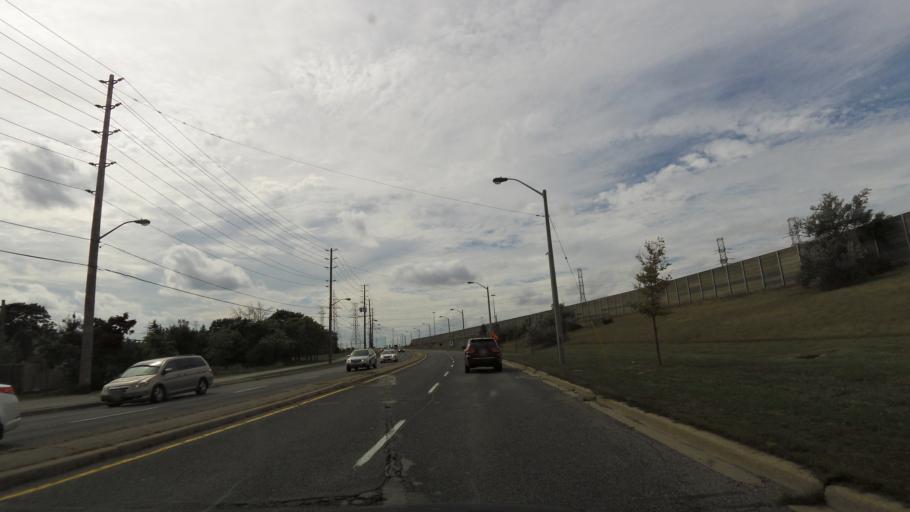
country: CA
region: Ontario
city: Etobicoke
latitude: 43.6705
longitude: -79.5799
